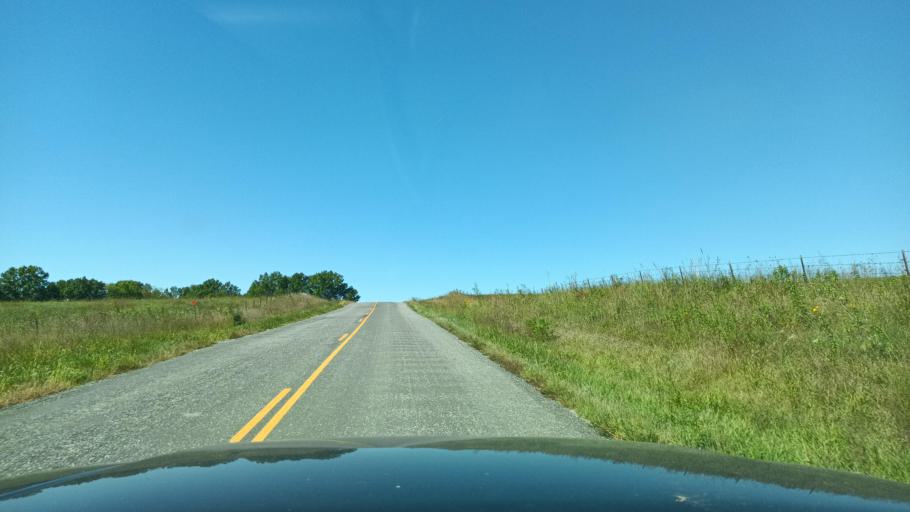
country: US
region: Missouri
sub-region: Adair County
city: Kirksville
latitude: 40.3302
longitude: -92.5363
